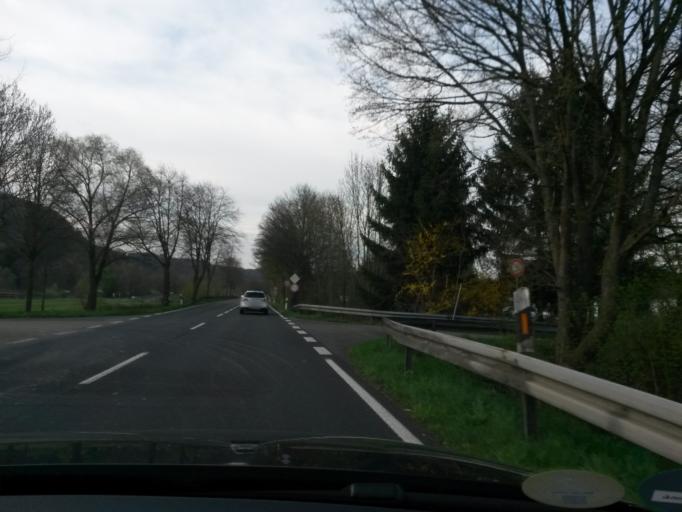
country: DE
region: North Rhine-Westphalia
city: Lohmar
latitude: 50.8821
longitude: 7.2488
